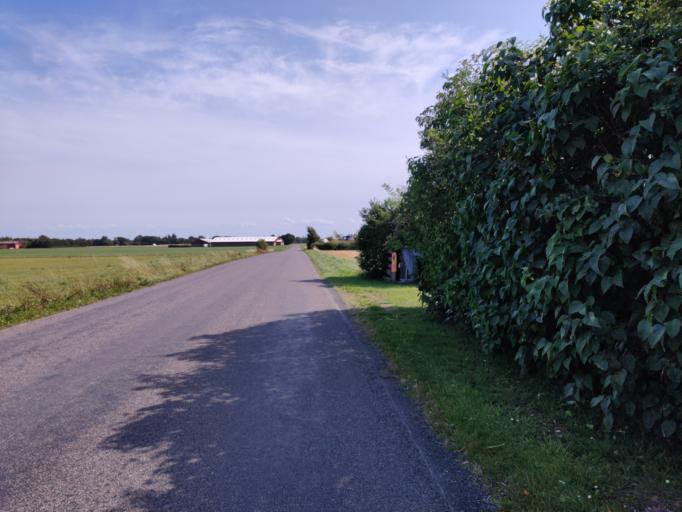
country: DK
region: Zealand
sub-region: Guldborgsund Kommune
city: Nykobing Falster
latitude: 54.6084
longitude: 11.9250
